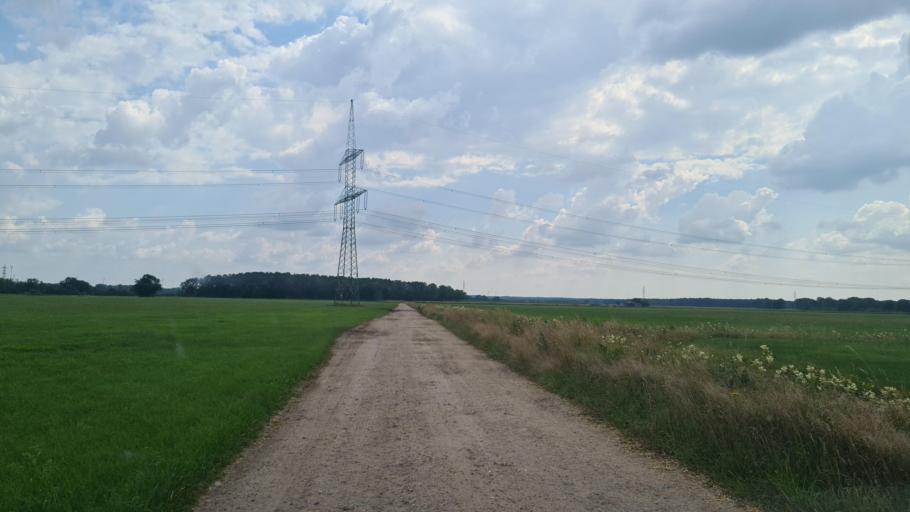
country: DE
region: Brandenburg
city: Sallgast
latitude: 51.6308
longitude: 13.8665
